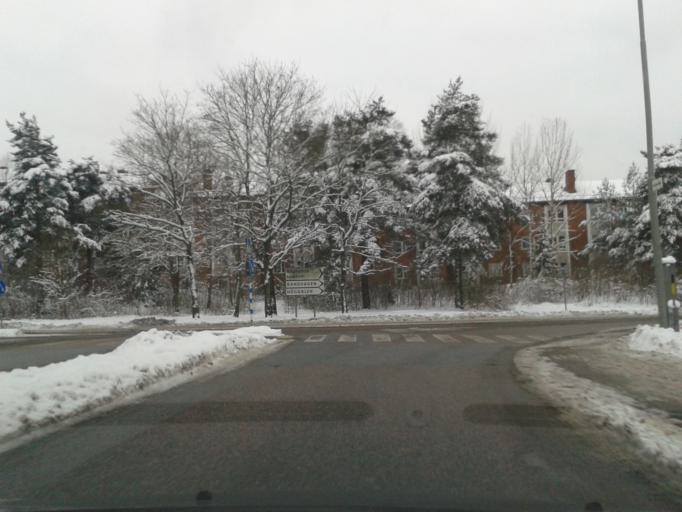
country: SE
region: Stockholm
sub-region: Stockholms Kommun
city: Arsta
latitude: 59.2686
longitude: 18.0542
